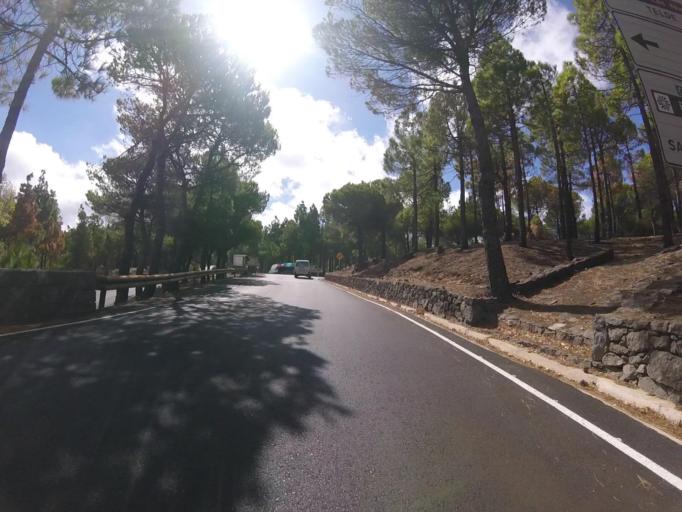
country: ES
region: Canary Islands
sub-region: Provincia de Las Palmas
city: Tejeda
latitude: 27.9776
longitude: -15.5804
